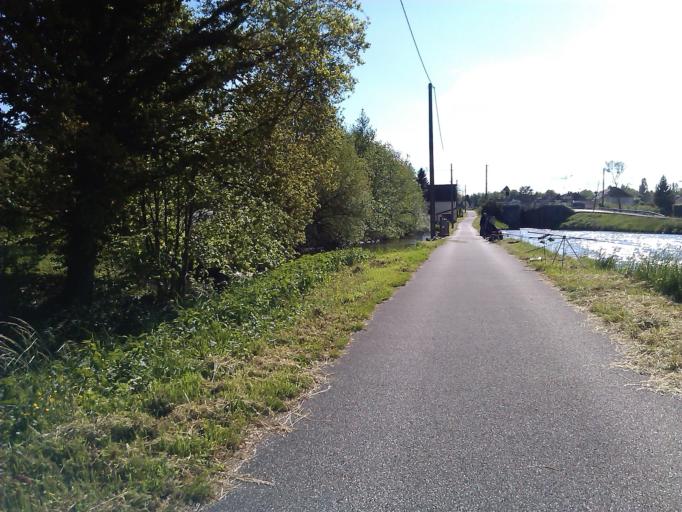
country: FR
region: Bourgogne
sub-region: Departement de Saone-et-Loire
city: Ecuisses
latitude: 46.7583
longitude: 4.5136
